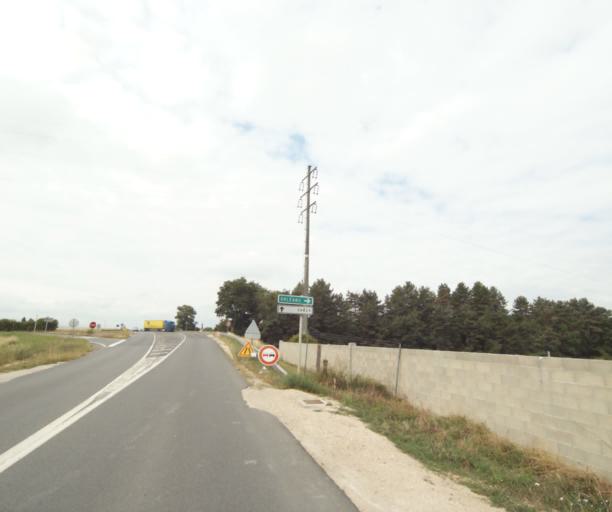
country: FR
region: Centre
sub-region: Departement du Loiret
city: Checy
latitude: 47.9092
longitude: 2.0350
